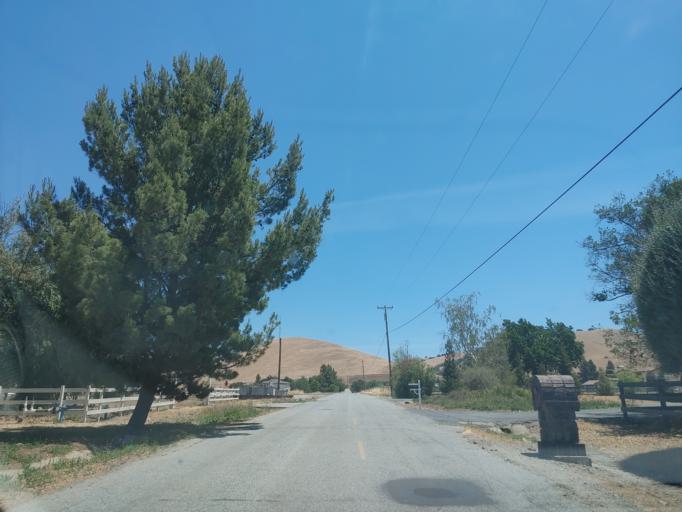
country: US
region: California
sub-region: San Benito County
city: Hollister
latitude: 36.9133
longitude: -121.3466
